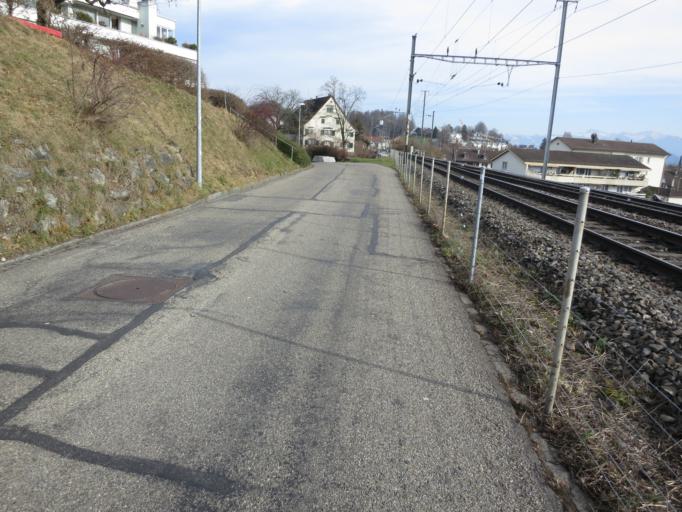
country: CH
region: Zurich
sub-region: Bezirk Meilen
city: Uerikon
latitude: 47.2361
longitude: 8.7552
